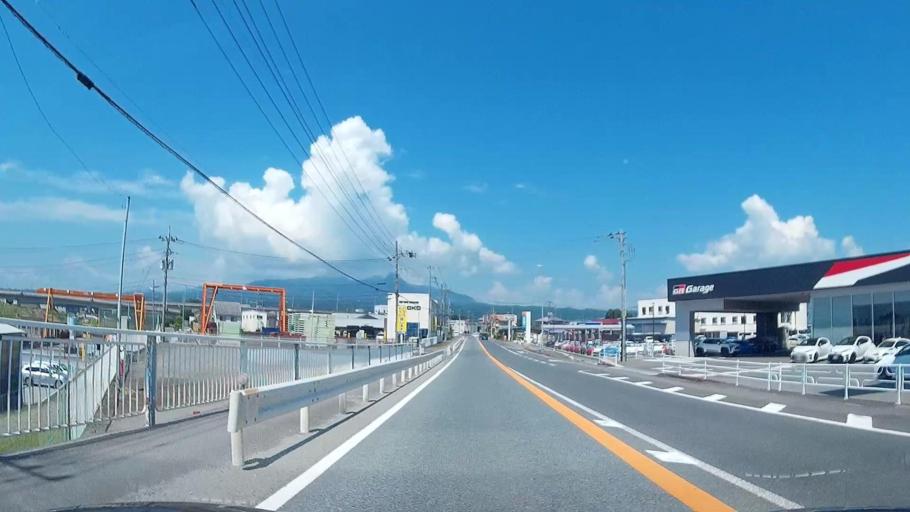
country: JP
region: Gunma
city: Shibukawa
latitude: 36.4646
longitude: 139.0325
